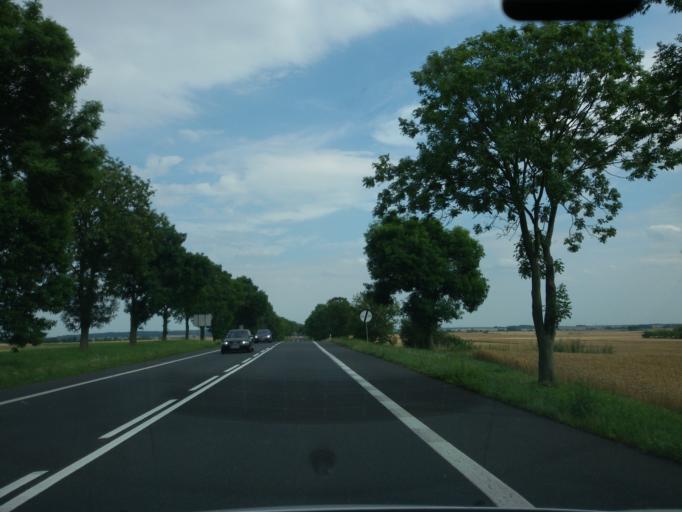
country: PL
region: Lower Silesian Voivodeship
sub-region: Powiat polkowicki
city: Gaworzyce
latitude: 51.6325
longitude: 15.9007
